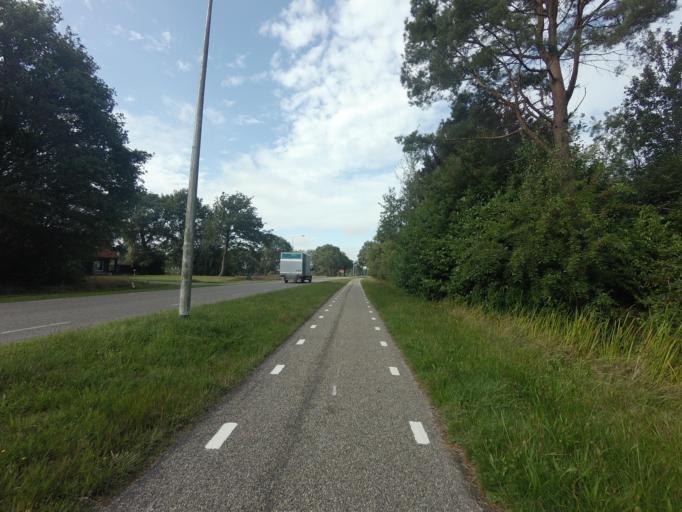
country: NL
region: Friesland
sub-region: Gemeente Heerenveen
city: Jubbega
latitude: 52.9808
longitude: 6.1281
